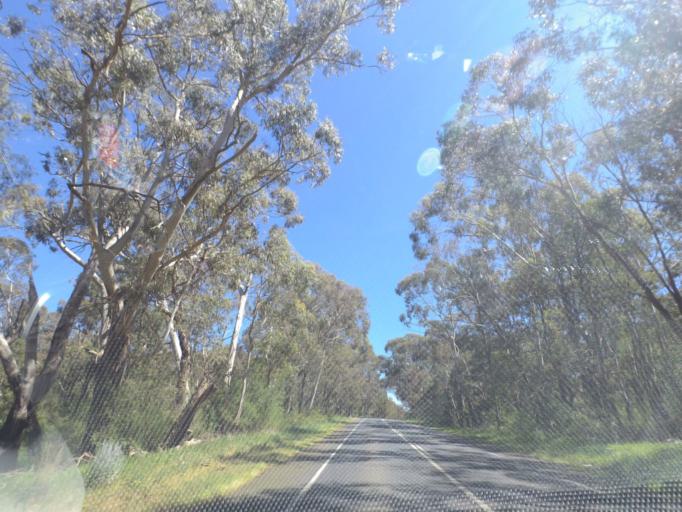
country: AU
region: Victoria
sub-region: Hume
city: Sunbury
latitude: -37.2949
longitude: 144.7992
